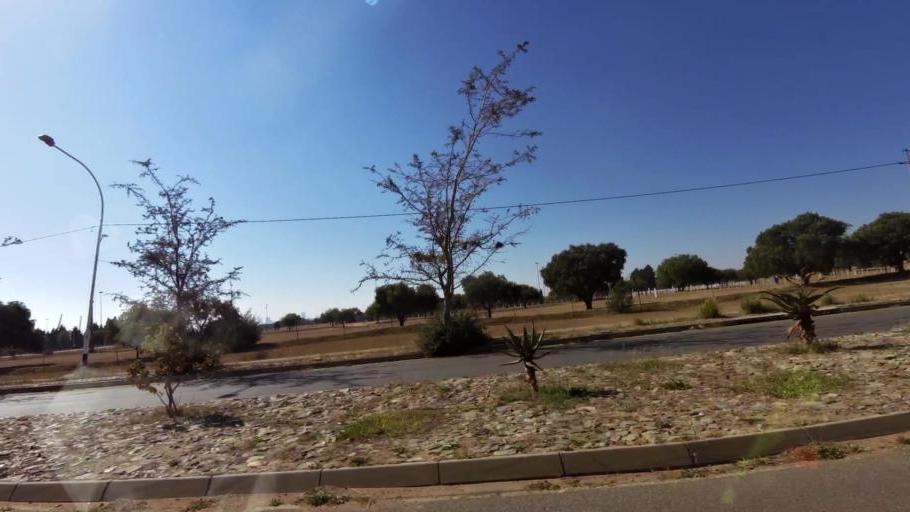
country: ZA
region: Gauteng
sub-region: City of Johannesburg Metropolitan Municipality
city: Johannesburg
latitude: -26.2466
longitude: 27.9753
